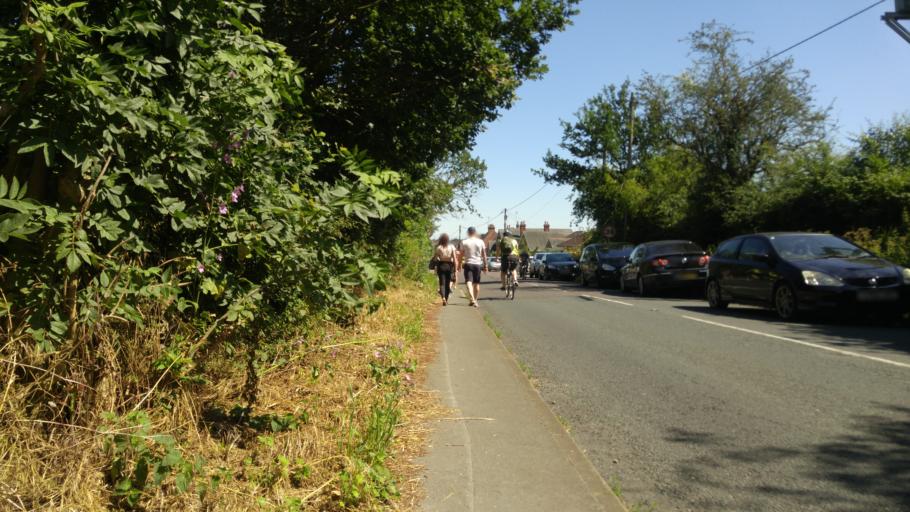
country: GB
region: England
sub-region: Essex
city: Rowhedge
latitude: 51.8603
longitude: 0.9413
